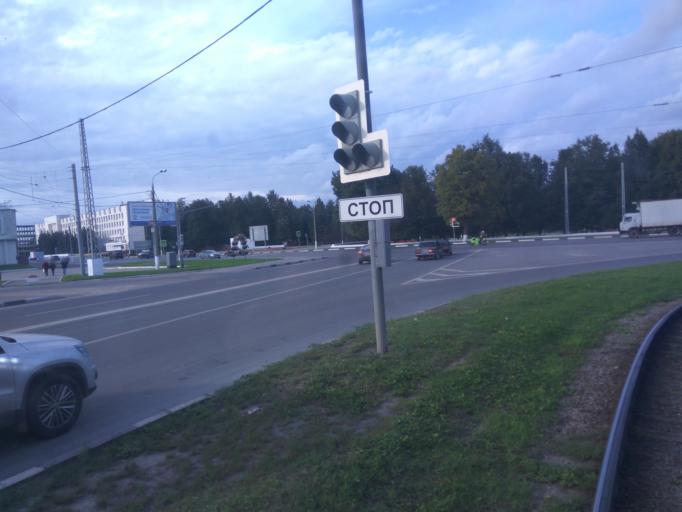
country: RU
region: Moskovskaya
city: Kolomna
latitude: 55.0934
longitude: 38.7687
